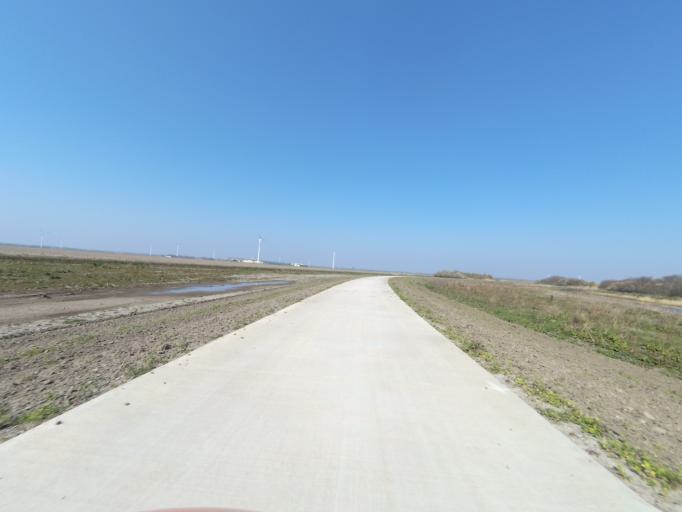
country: NL
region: Utrecht
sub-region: Gemeente Bunschoten
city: Spakenburg
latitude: 52.3725
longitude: 5.3738
